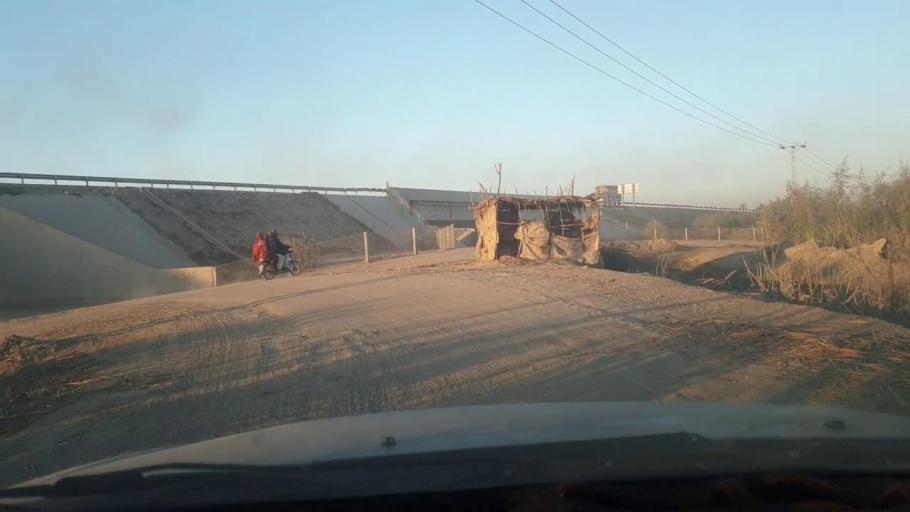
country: PK
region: Sindh
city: Ghotki
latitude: 28.0437
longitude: 69.3251
